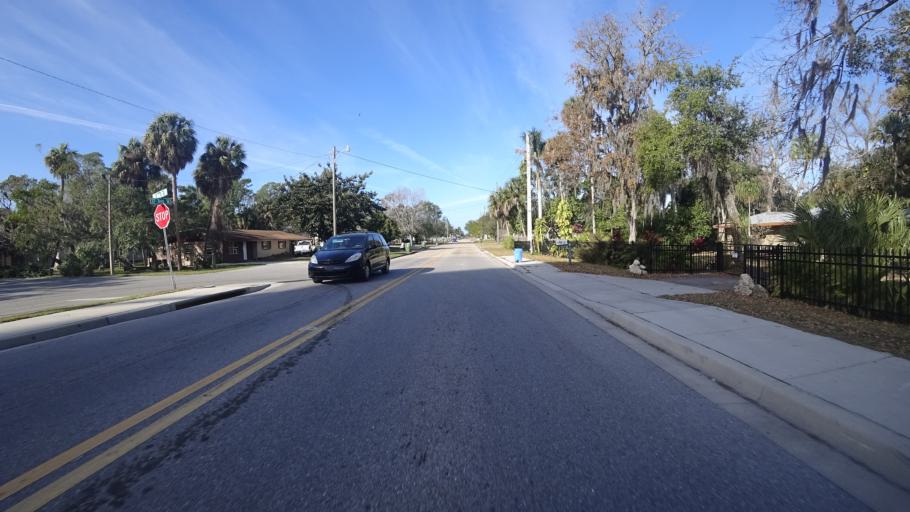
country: US
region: Florida
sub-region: Manatee County
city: Bradenton
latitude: 27.4846
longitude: -82.5813
